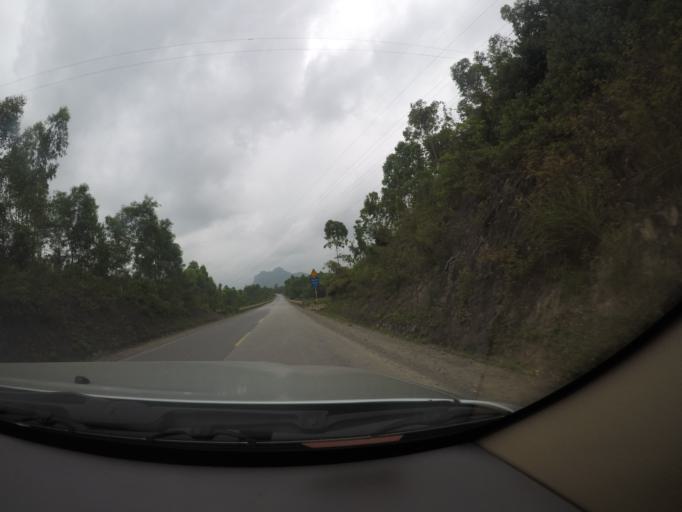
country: VN
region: Quang Binh
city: Quan Hau
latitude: 17.3324
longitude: 106.6251
